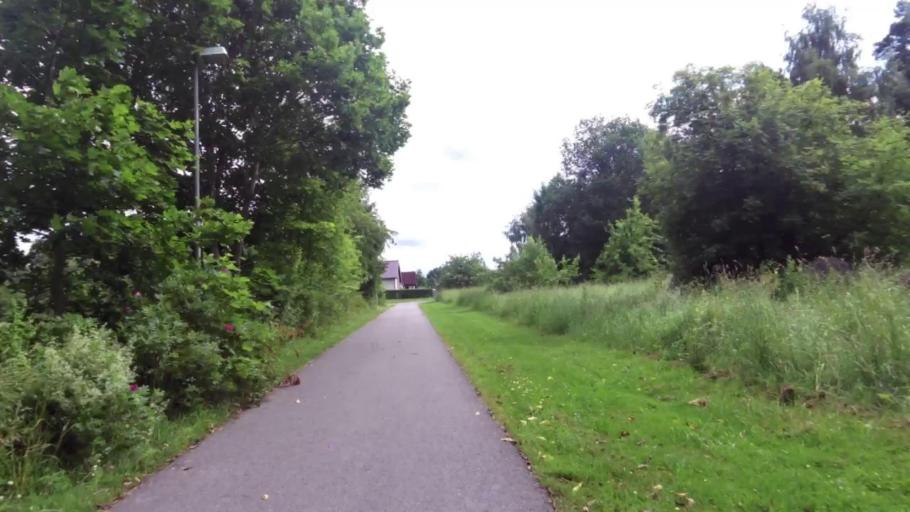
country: SE
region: OEstergoetland
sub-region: Linkopings Kommun
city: Malmslatt
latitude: 58.4156
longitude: 15.5583
